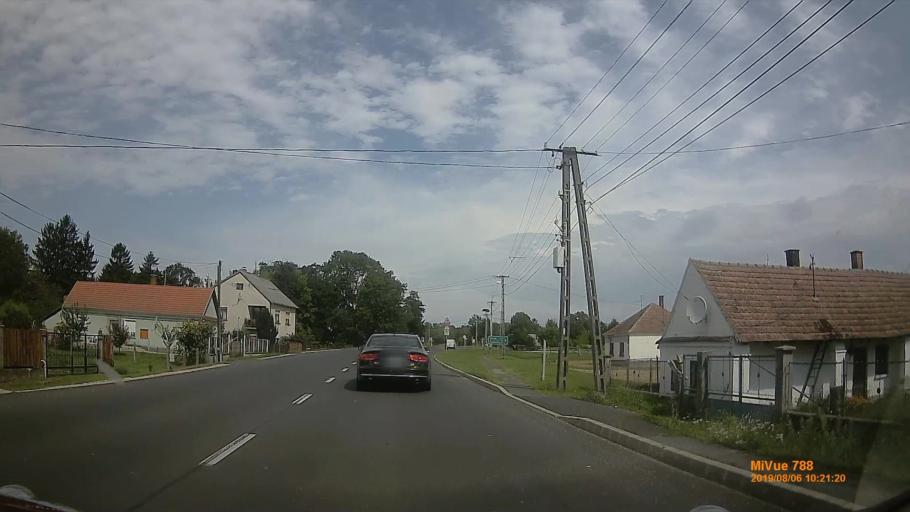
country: HU
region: Vas
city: Vasvar
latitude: 47.0654
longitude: 16.7444
